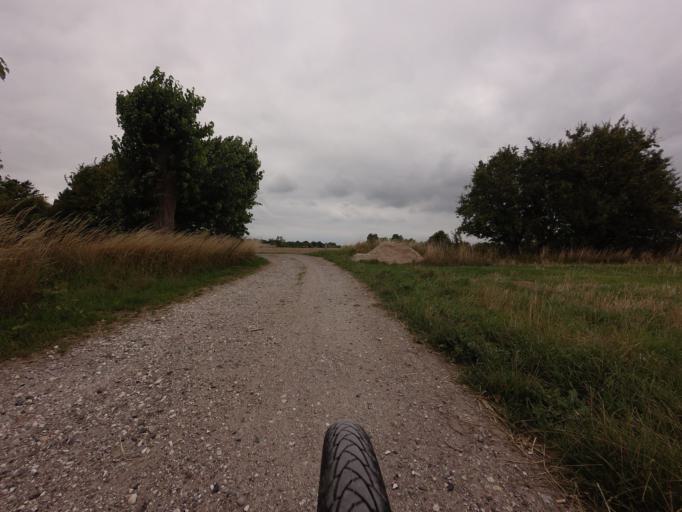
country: DK
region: Zealand
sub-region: Stevns Kommune
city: Store Heddinge
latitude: 55.3311
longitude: 12.4492
